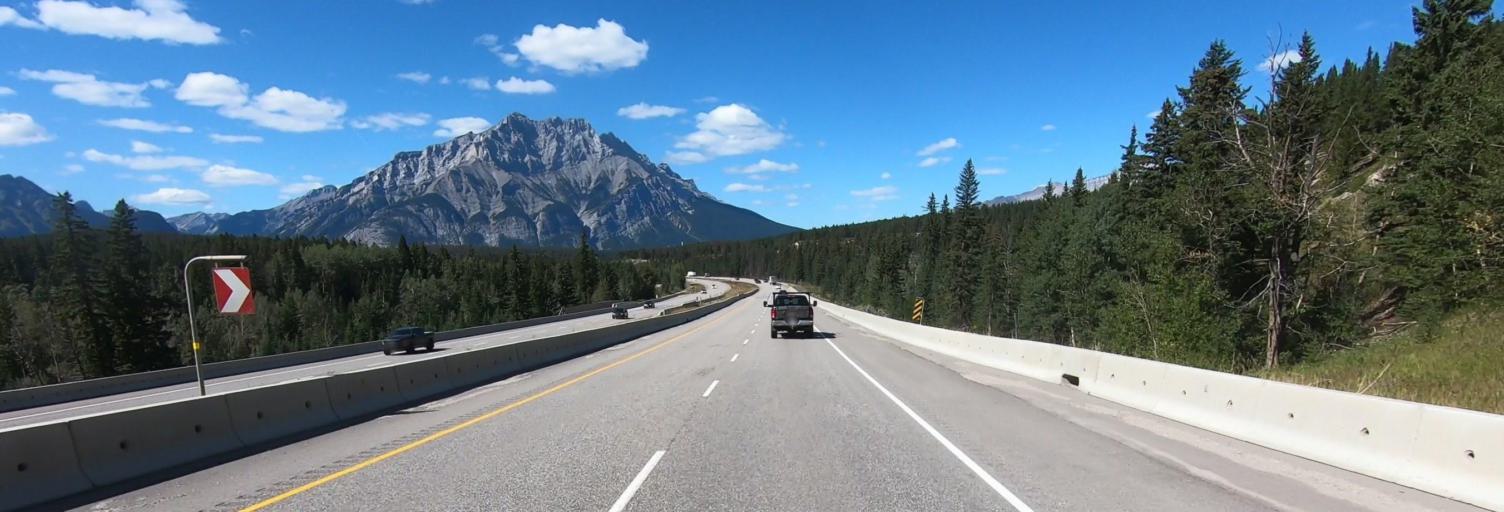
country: CA
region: Alberta
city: Banff
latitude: 51.1714
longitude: -115.4676
